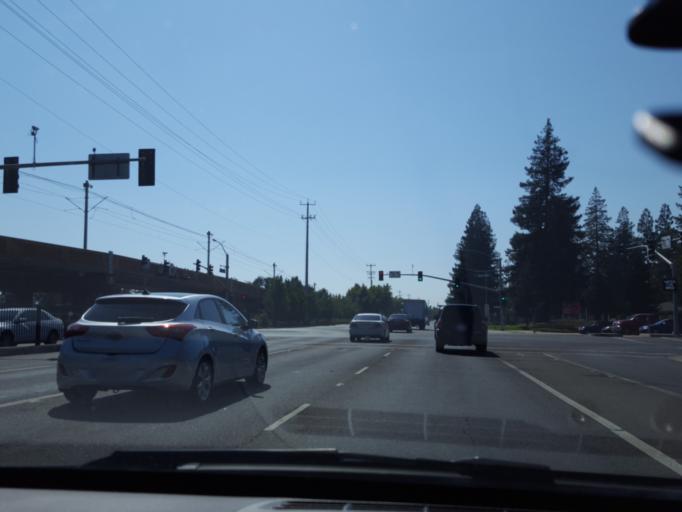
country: US
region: California
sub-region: Sacramento County
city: Rosemont
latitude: 38.5535
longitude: -121.3746
